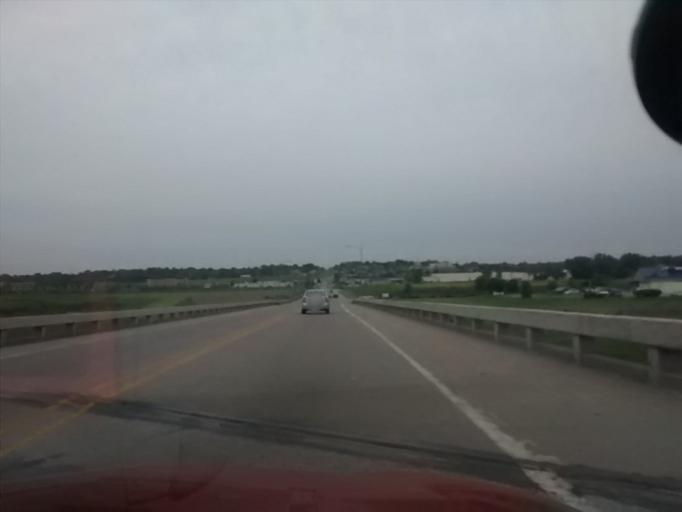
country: US
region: Nebraska
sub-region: Sarpy County
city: Offutt Air Force Base
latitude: 41.1495
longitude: -95.9670
